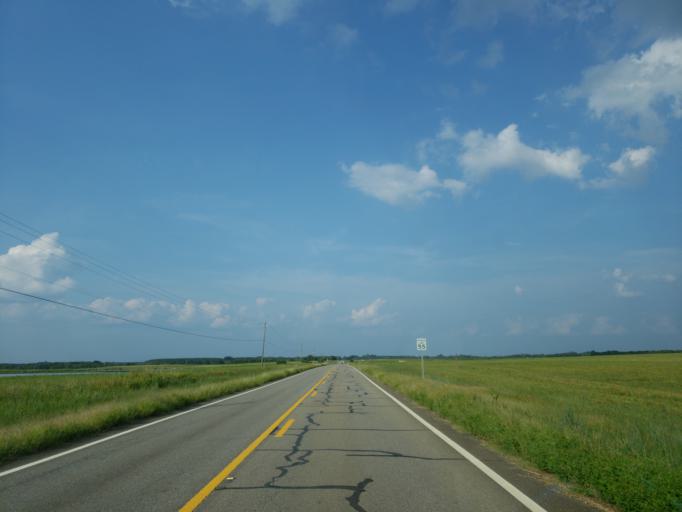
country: US
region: Alabama
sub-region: Greene County
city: Eutaw
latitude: 32.8057
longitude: -87.9540
